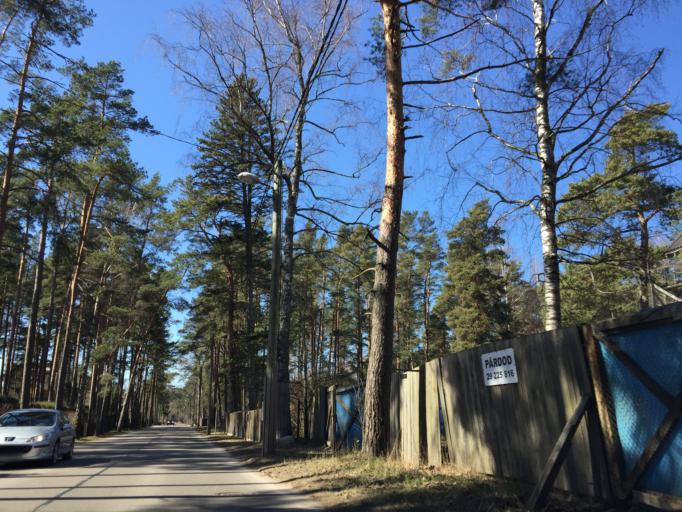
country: LV
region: Jurmala
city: Jurmala
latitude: 56.9430
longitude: 23.7085
